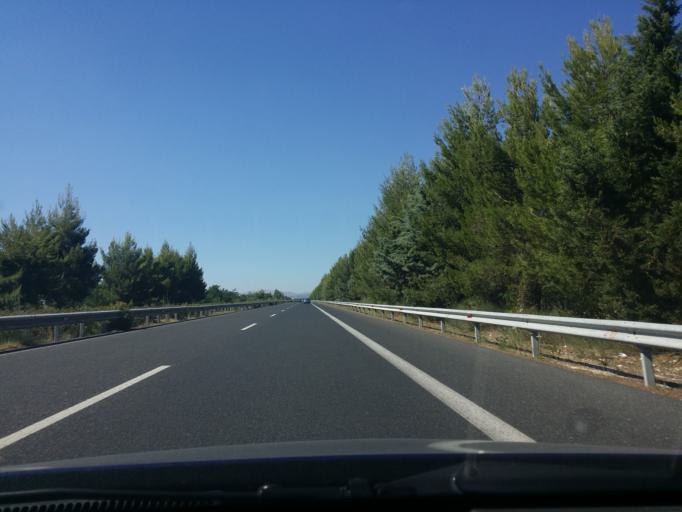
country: GR
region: Peloponnese
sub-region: Nomos Arkadias
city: Tripoli
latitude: 37.5446
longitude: 22.4170
